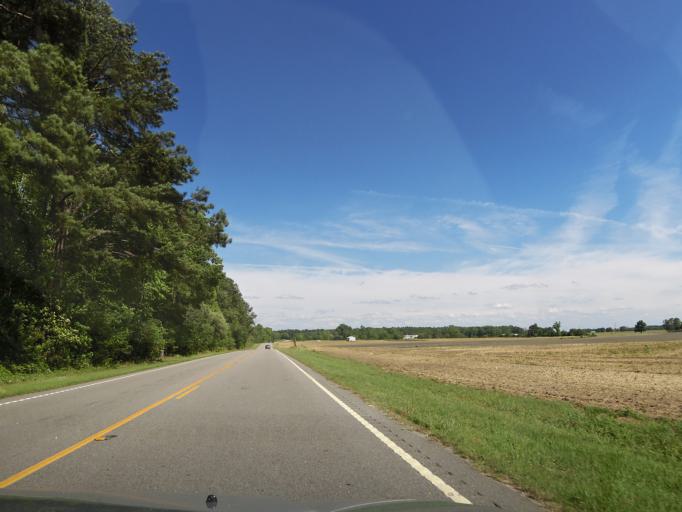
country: US
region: South Carolina
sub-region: Barnwell County
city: Blackville
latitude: 33.3699
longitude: -81.3389
